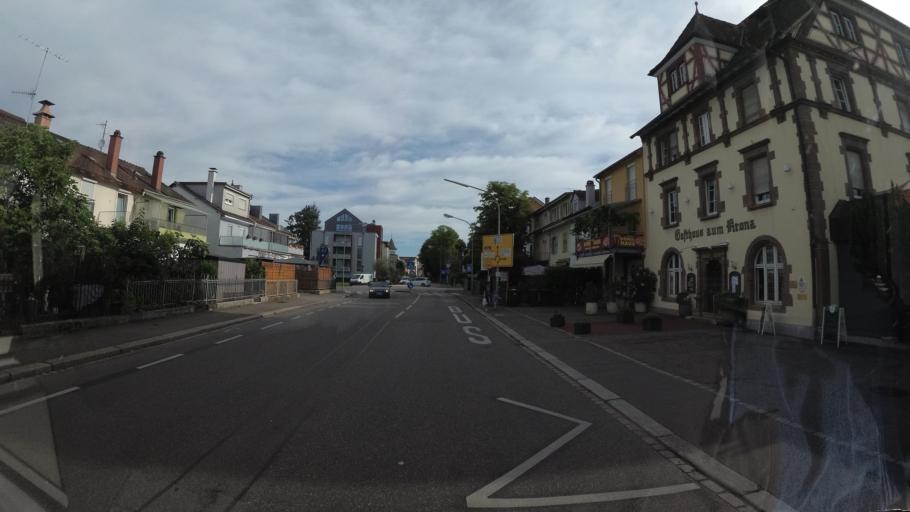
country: DE
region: Baden-Wuerttemberg
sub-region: Freiburg Region
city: Loerrach
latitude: 47.6062
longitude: 7.6597
